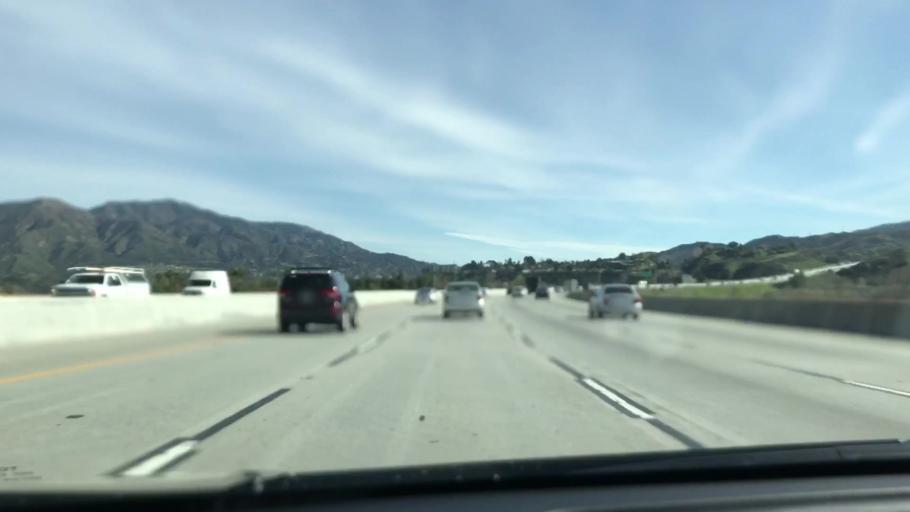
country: US
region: California
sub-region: Los Angeles County
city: Burbank
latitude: 34.2711
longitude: -118.3415
